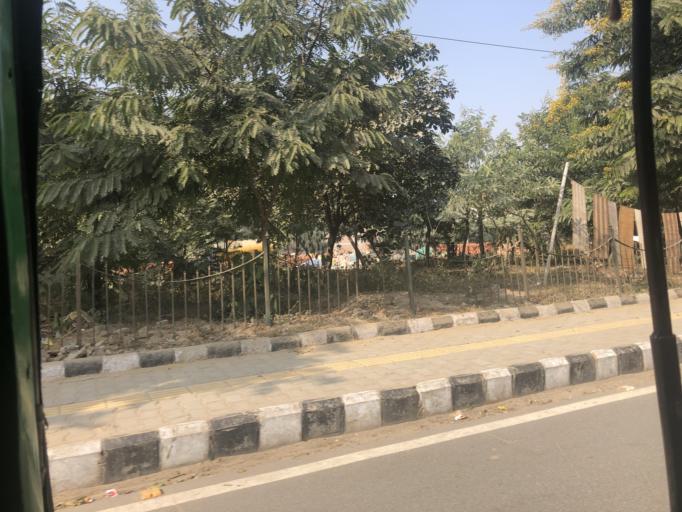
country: IN
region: Haryana
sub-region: Gurgaon
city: Gurgaon
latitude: 28.4259
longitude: 77.0911
